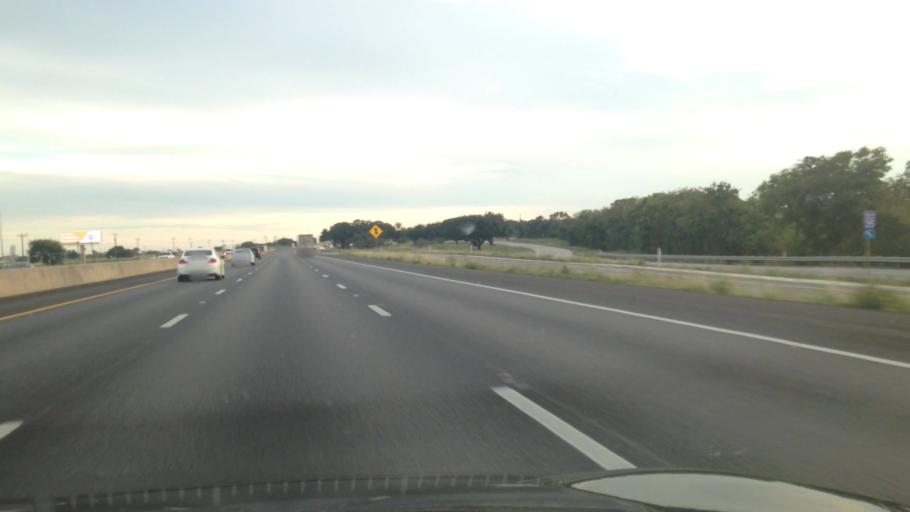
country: US
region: Texas
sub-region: Hays County
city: Kyle
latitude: 29.9560
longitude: -97.8780
